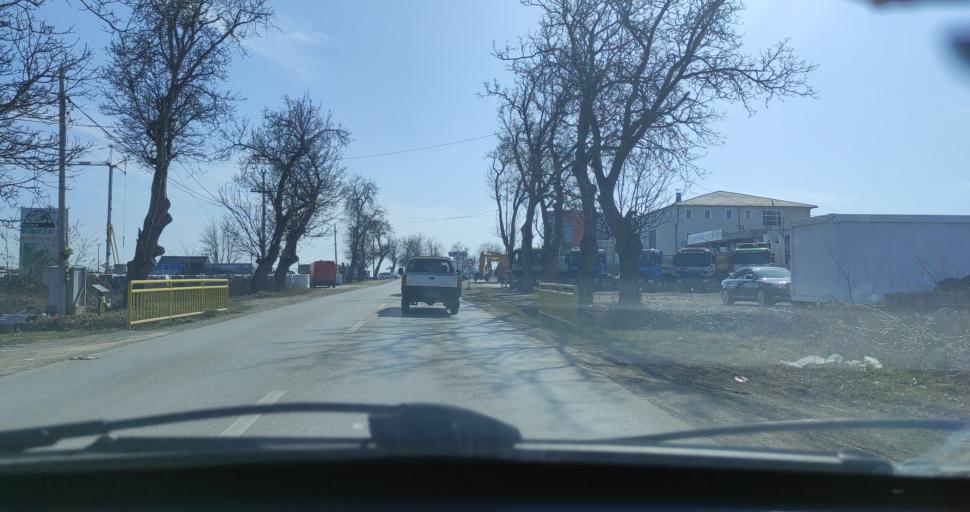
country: XK
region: Pec
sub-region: Komuna e Pejes
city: Peje
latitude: 42.6334
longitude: 20.3025
